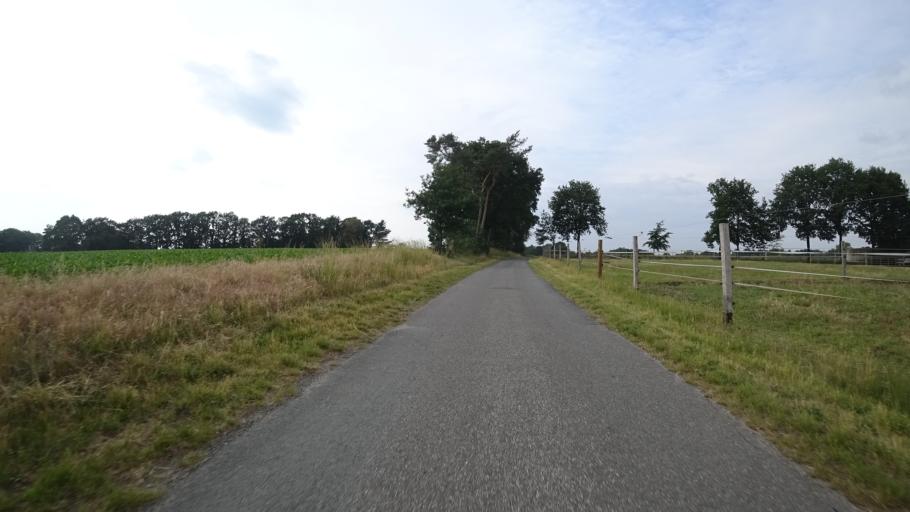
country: DE
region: North Rhine-Westphalia
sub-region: Regierungsbezirk Detmold
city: Guetersloh
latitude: 51.9508
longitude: 8.3702
